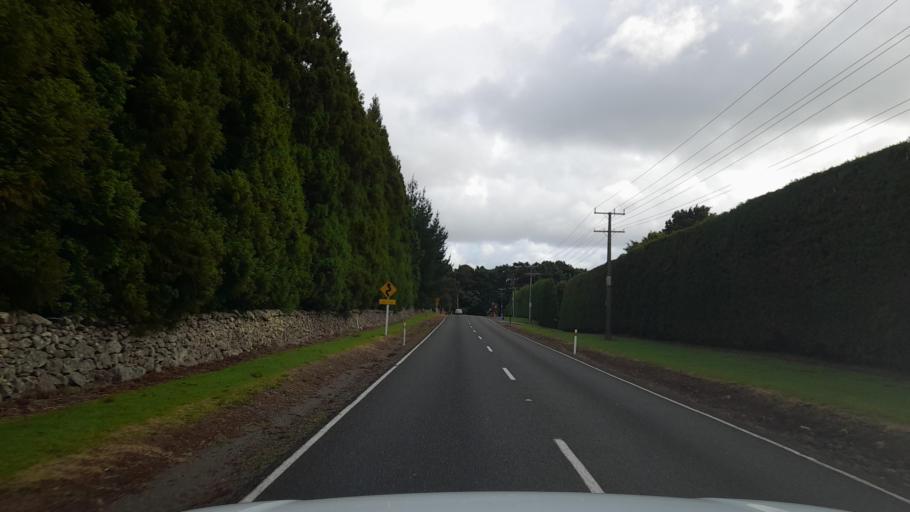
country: NZ
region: Northland
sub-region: Whangarei
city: Maungatapere
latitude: -35.7514
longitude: 174.2520
